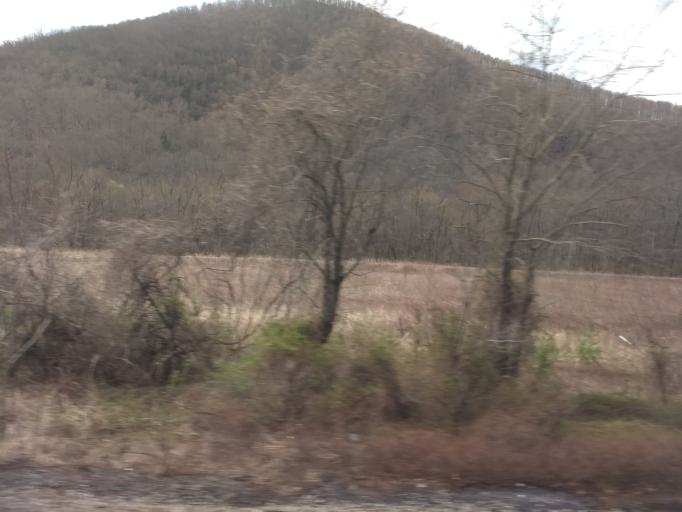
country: US
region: Pennsylvania
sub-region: Huntingdon County
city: Huntingdon
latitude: 40.4463
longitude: -77.9573
